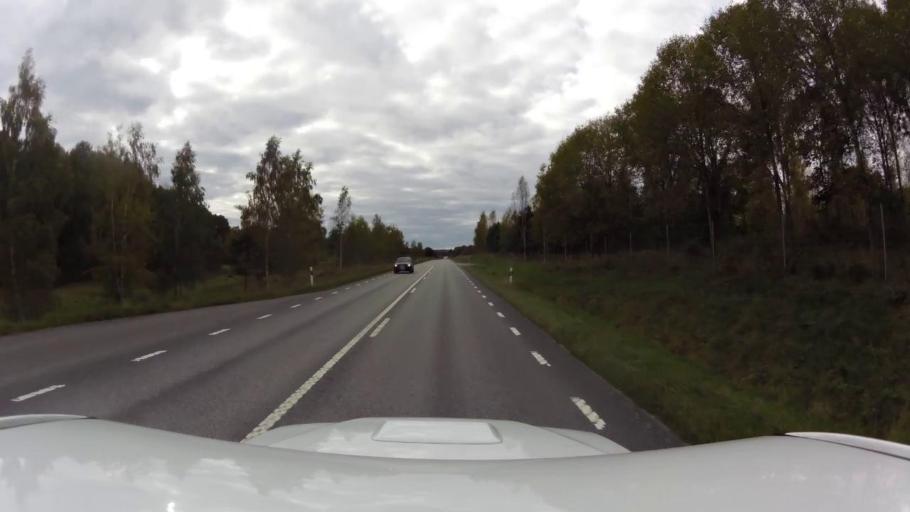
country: SE
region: OEstergoetland
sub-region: Kinda Kommun
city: Rimforsa
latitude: 58.2052
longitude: 15.6686
